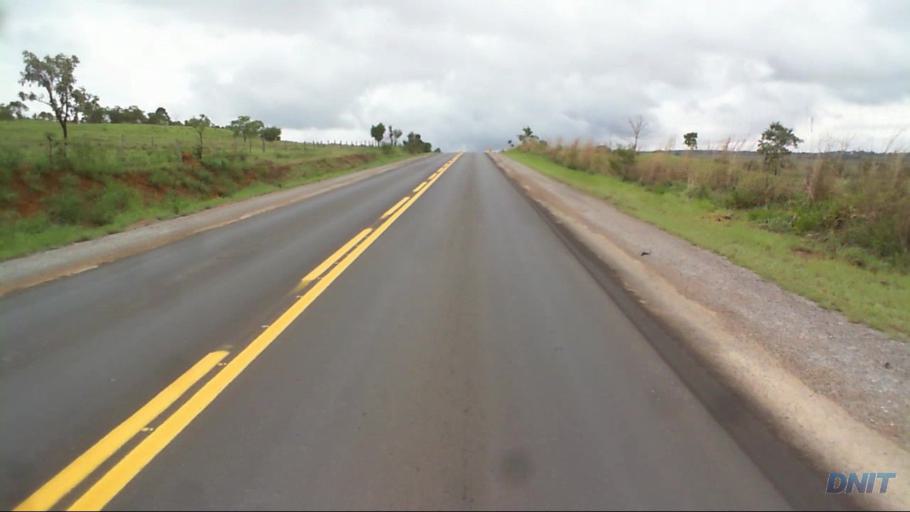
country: BR
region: Goias
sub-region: Padre Bernardo
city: Padre Bernardo
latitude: -15.2184
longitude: -48.5161
